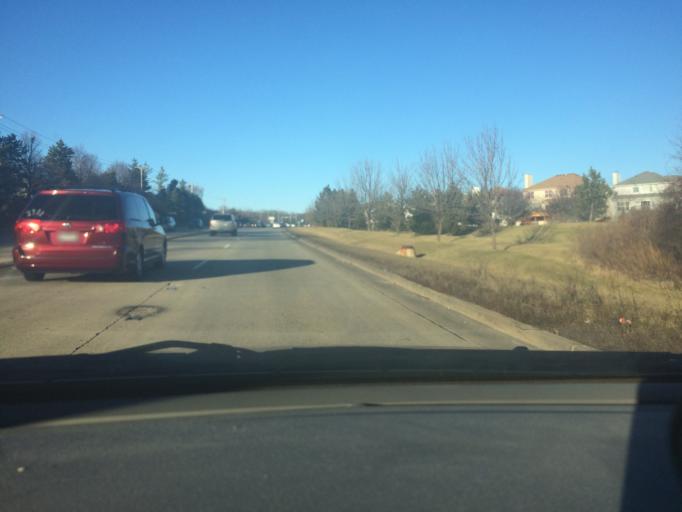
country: US
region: Illinois
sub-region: Cook County
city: Streamwood
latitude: 42.0274
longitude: -88.2028
